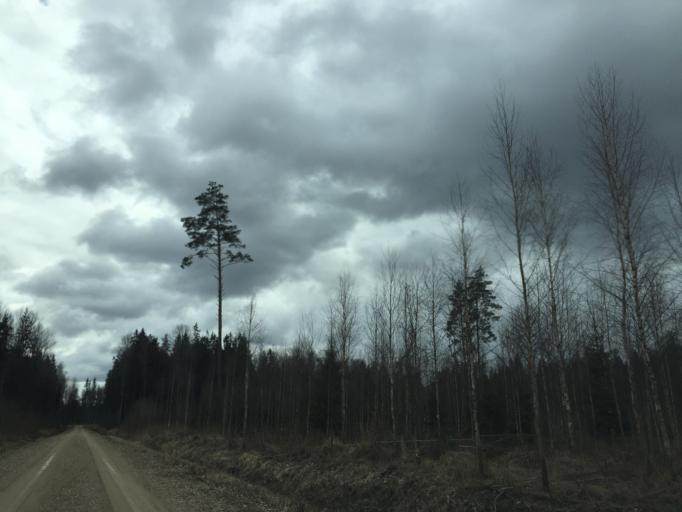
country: LV
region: Akniste
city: Akniste
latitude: 56.0800
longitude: 25.7618
